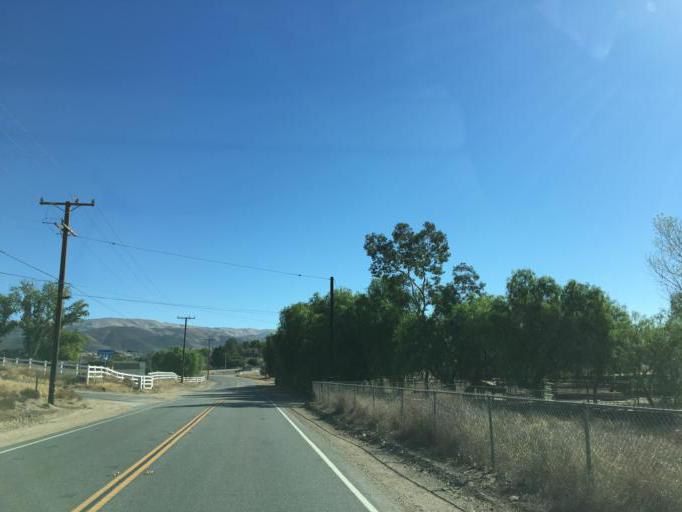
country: US
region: California
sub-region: Los Angeles County
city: Agua Dulce
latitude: 34.5056
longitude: -118.3221
